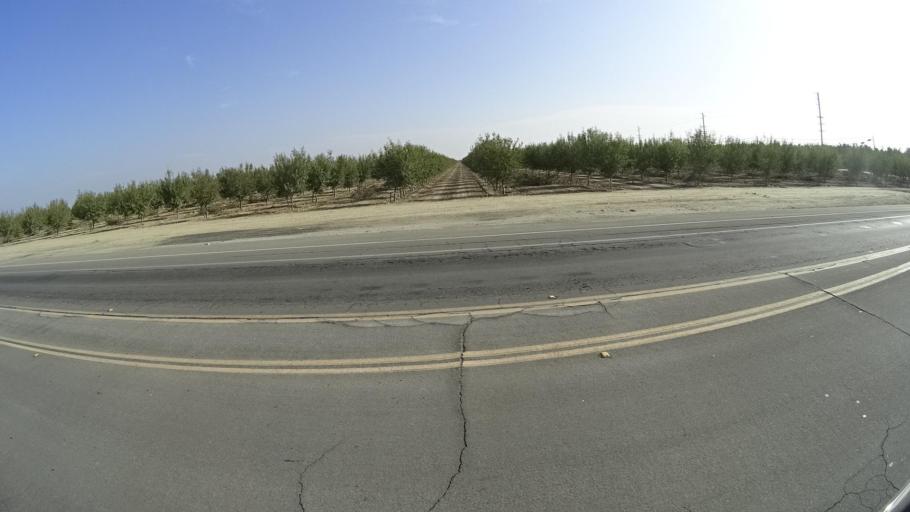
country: US
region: California
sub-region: Kern County
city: Delano
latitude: 35.7768
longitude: -119.2232
